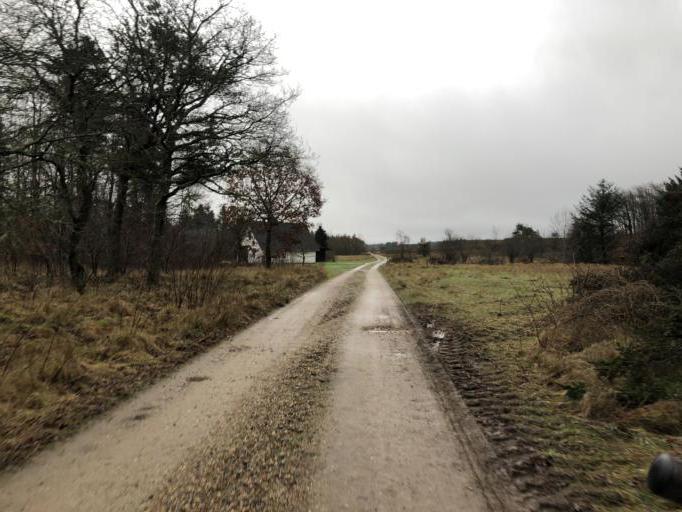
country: DK
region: Central Jutland
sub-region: Holstebro Kommune
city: Ulfborg
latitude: 56.2880
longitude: 8.4590
